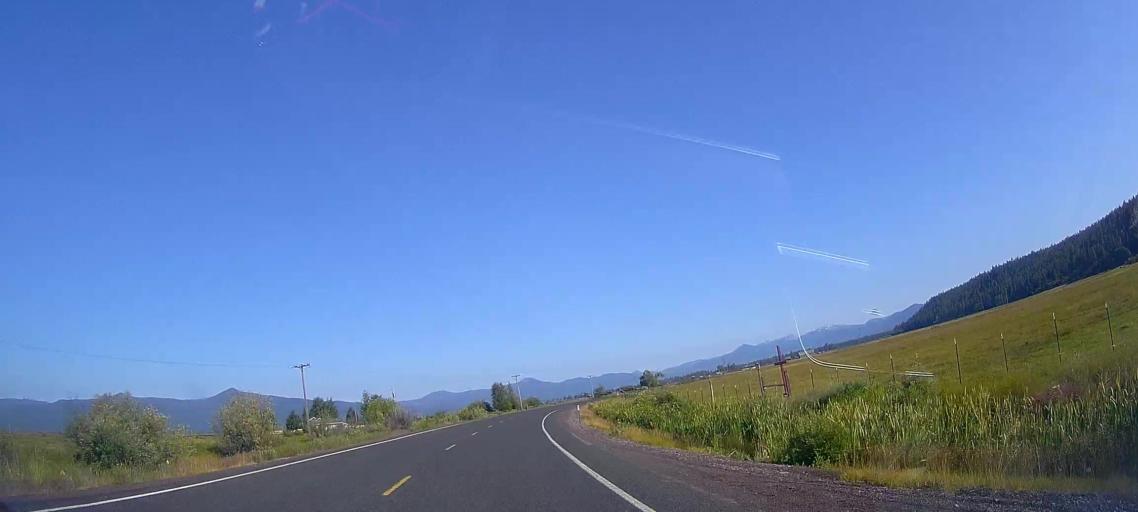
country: US
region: Oregon
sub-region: Klamath County
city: Klamath Falls
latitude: 42.6469
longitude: -121.9529
